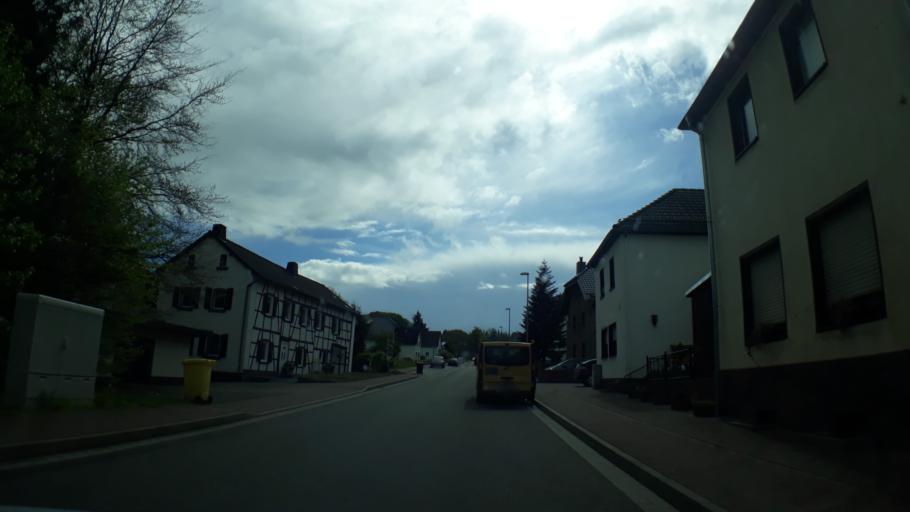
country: DE
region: North Rhine-Westphalia
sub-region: Regierungsbezirk Koln
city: Kall
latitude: 50.5149
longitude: 6.5470
